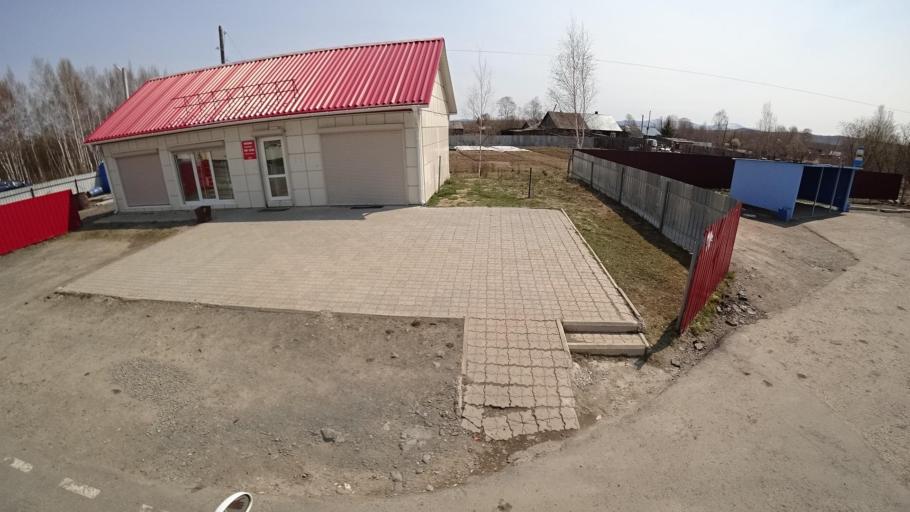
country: RU
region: Khabarovsk Krai
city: Selikhino
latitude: 50.3901
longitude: 137.3739
